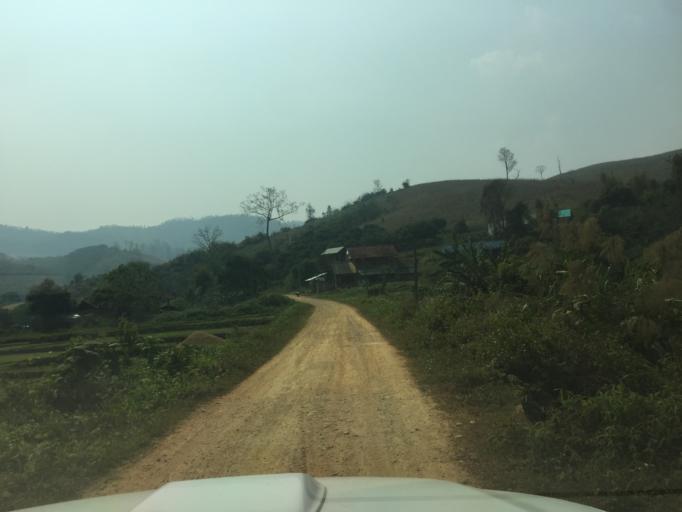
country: TH
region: Phayao
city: Phu Sang
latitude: 19.5832
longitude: 100.5261
